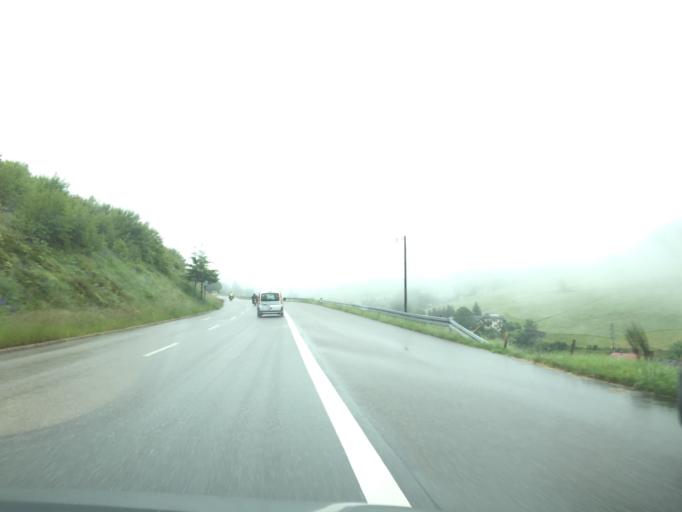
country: DE
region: Baden-Wuerttemberg
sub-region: Freiburg Region
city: Todtnau
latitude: 47.8458
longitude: 7.9378
